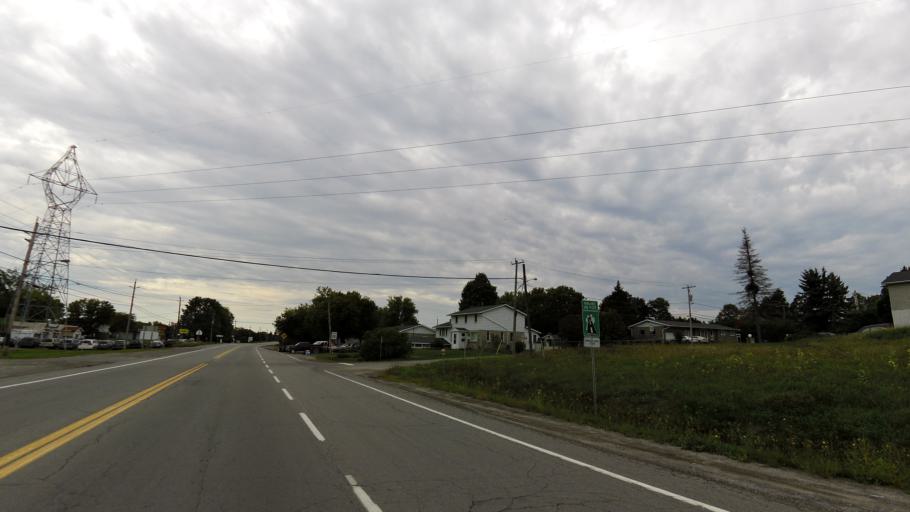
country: CA
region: Ontario
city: Ottawa
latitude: 45.2781
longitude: -75.5691
